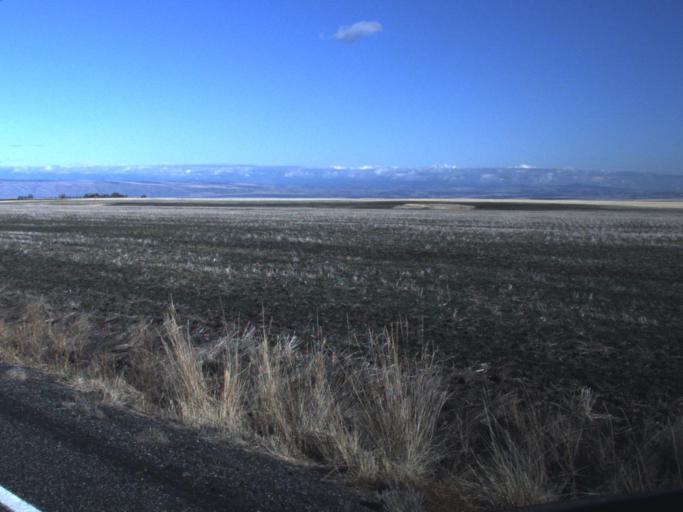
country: US
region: Washington
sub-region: Asotin County
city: Asotin
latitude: 46.2178
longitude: -117.0703
